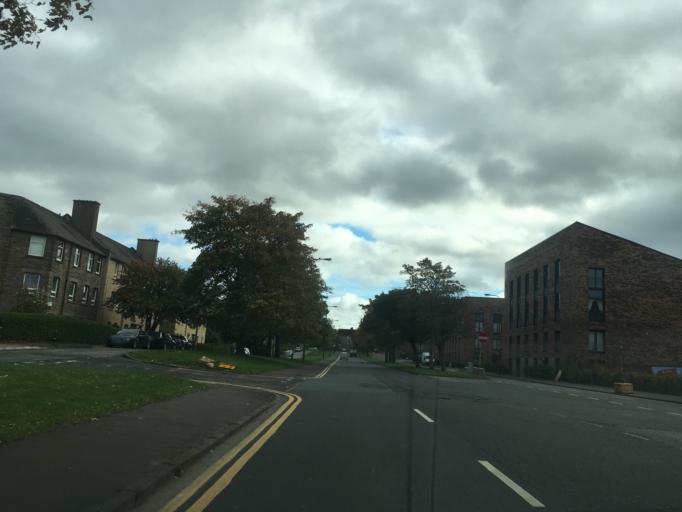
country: GB
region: Scotland
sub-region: Edinburgh
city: Edinburgh
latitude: 55.9696
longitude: -3.2505
